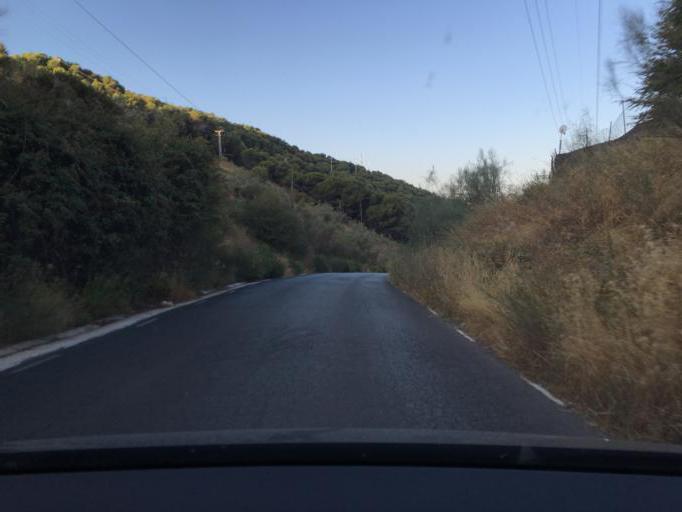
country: ES
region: Andalusia
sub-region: Provincia de Granada
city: Granada
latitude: 37.1940
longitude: -3.5825
